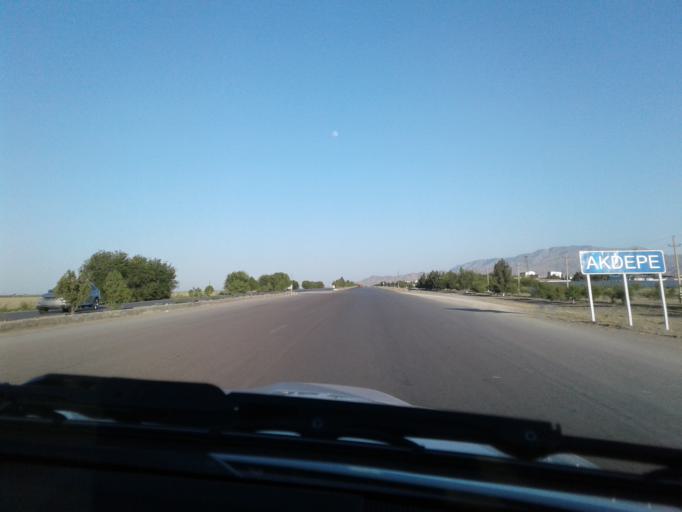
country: TM
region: Ahal
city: Baharly
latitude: 38.3257
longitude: 57.5878
